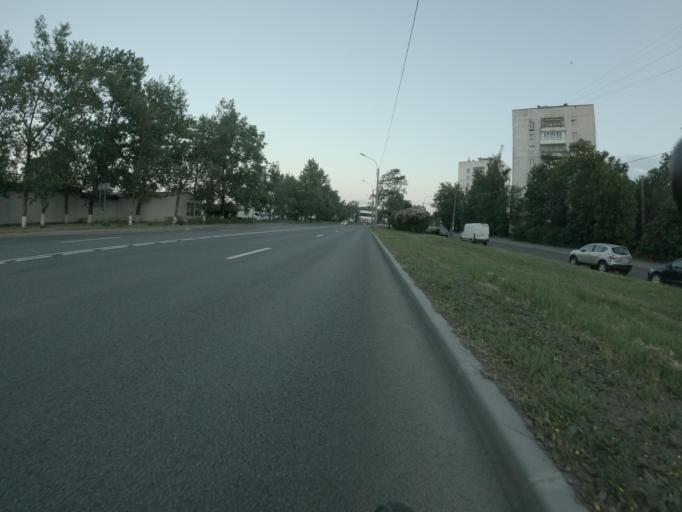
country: RU
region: St.-Petersburg
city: Dachnoye
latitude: 59.8470
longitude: 30.2802
